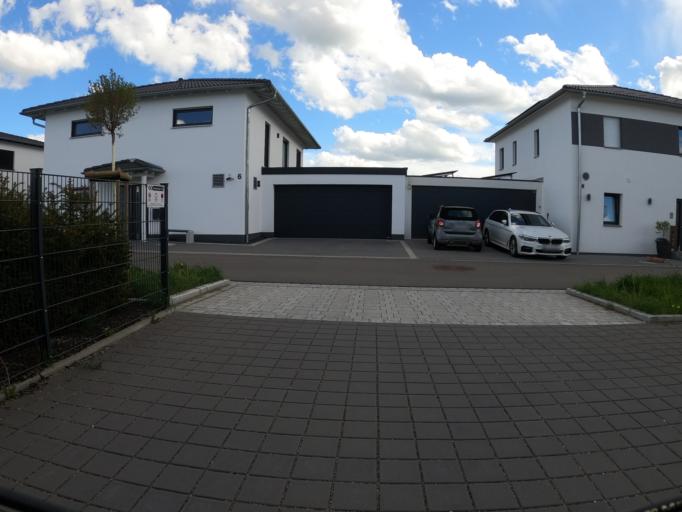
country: DE
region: Bavaria
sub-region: Swabia
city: Leipheim
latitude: 48.4516
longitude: 10.2341
